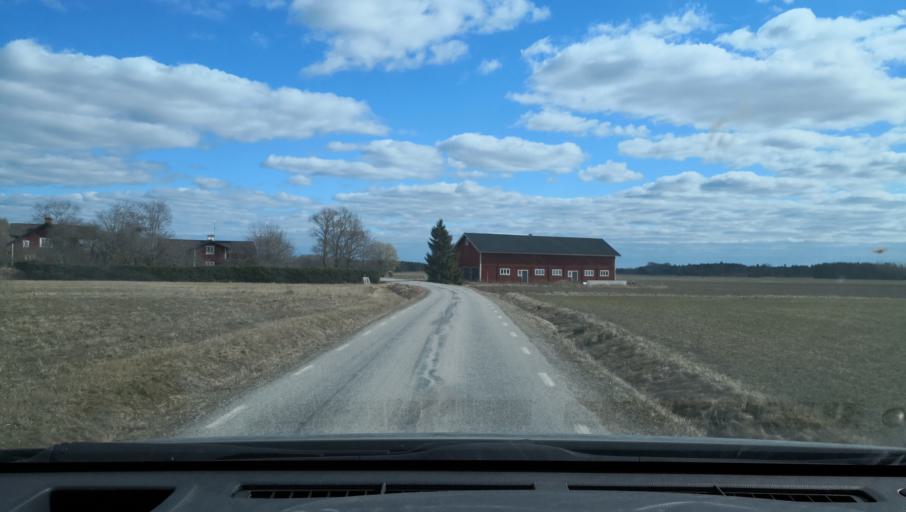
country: SE
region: Vaestmanland
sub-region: Sala Kommun
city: Sala
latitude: 59.8595
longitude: 16.6036
